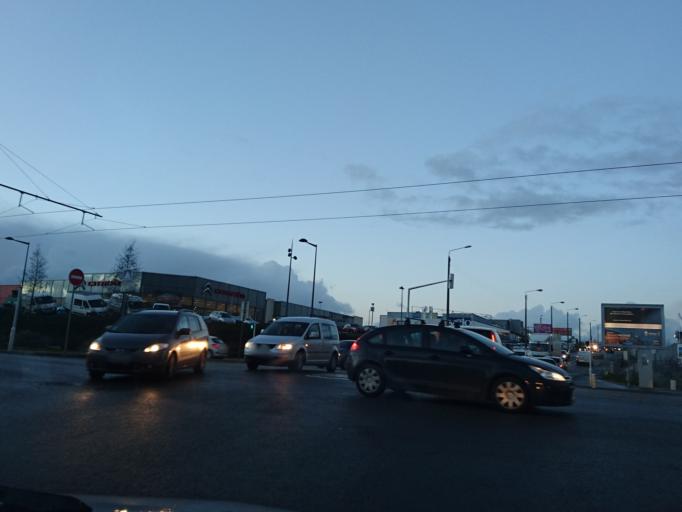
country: FR
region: Brittany
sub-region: Departement du Finistere
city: Brest
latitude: 48.4164
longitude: -4.4627
